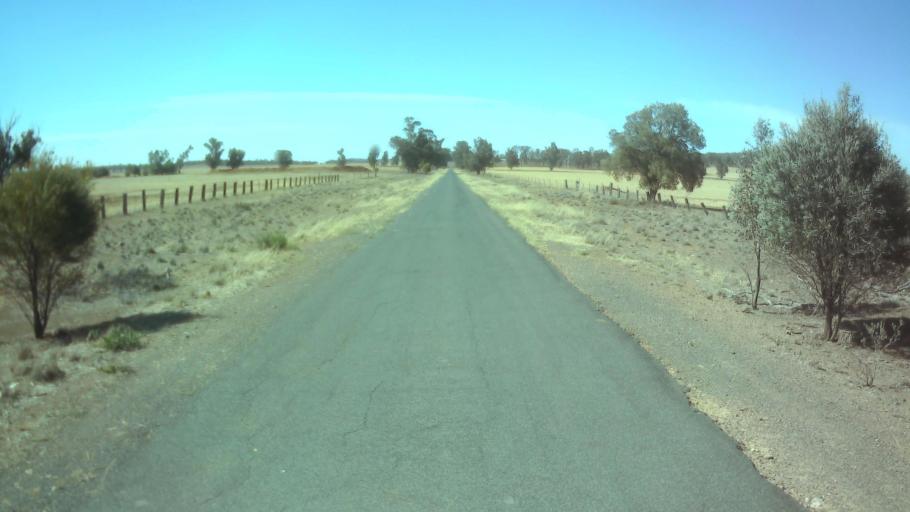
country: AU
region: New South Wales
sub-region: Forbes
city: Forbes
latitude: -33.7396
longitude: 147.7410
